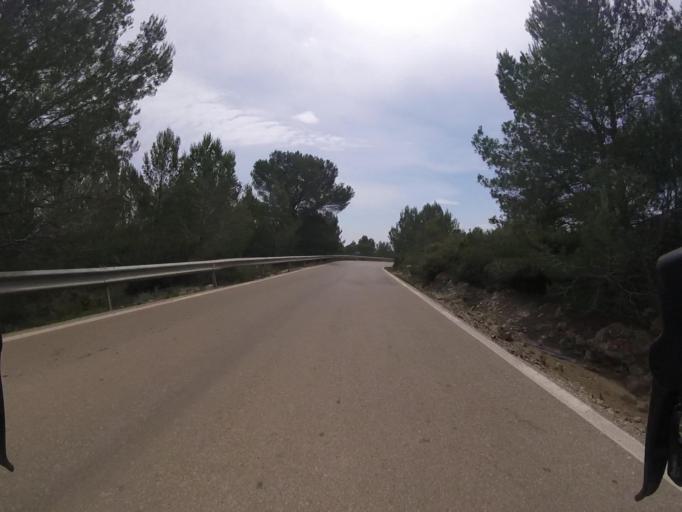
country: ES
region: Valencia
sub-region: Provincia de Castello
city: Cabanes
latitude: 40.1586
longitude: 0.0833
